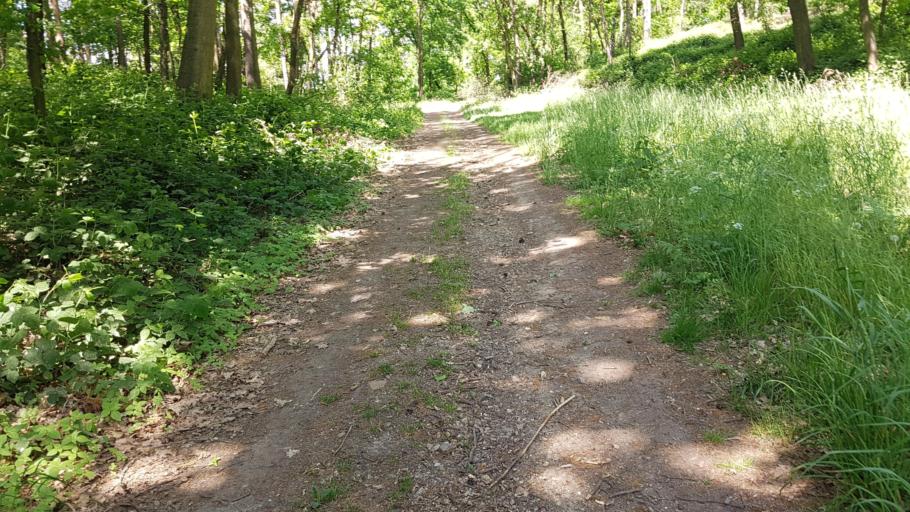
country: DE
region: Brandenburg
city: Grosskmehlen
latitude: 51.3657
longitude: 13.7061
